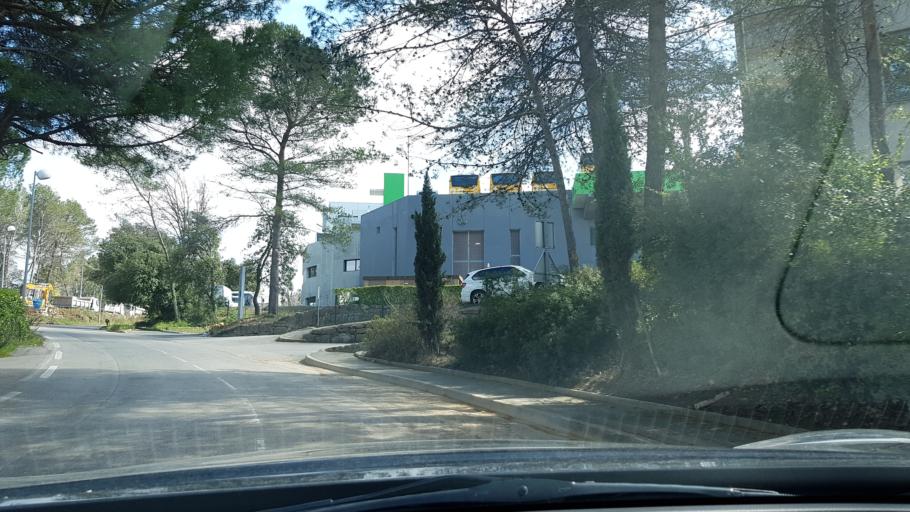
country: FR
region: Provence-Alpes-Cote d'Azur
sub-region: Departement des Alpes-Maritimes
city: Biot
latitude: 43.6085
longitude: 7.0738
